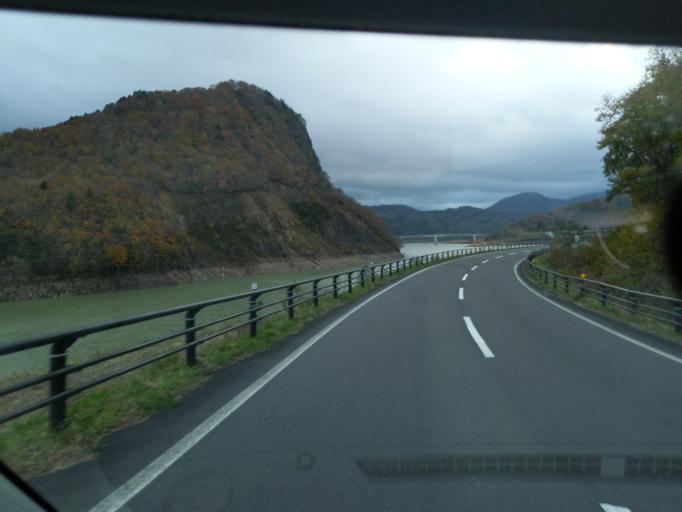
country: JP
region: Iwate
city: Mizusawa
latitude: 39.1122
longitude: 140.8912
